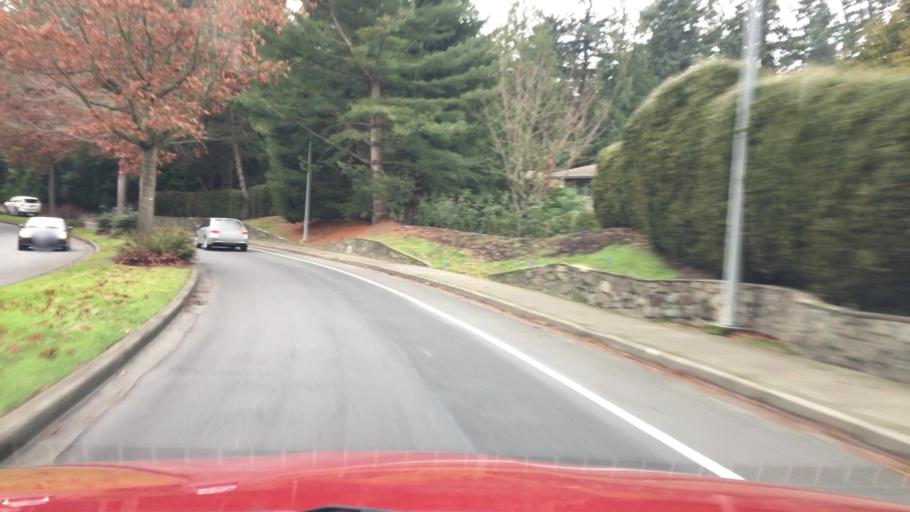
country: CA
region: British Columbia
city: Victoria
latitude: 48.5014
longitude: -123.3645
